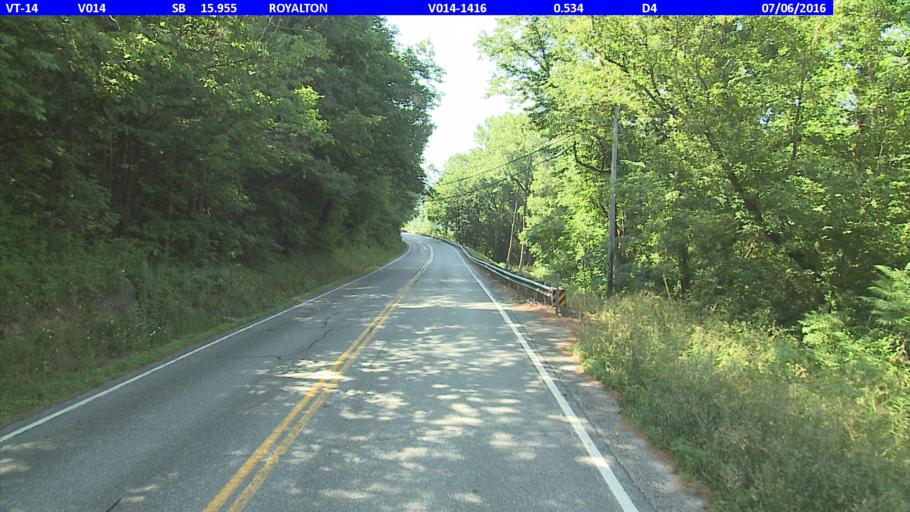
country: US
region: Vermont
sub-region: Windsor County
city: Woodstock
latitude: 43.8021
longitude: -72.5014
